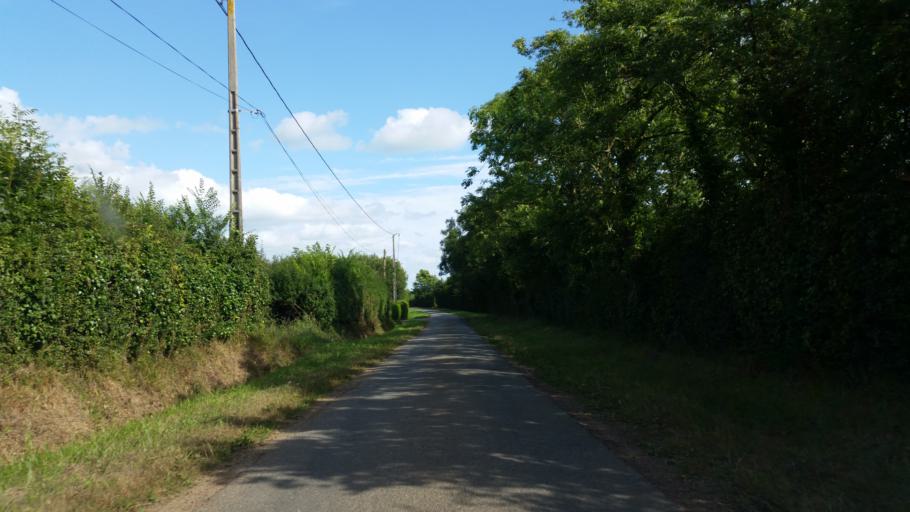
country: FR
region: Lower Normandy
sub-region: Departement de la Manche
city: Sainte-Mere-Eglise
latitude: 49.4598
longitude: -1.2989
